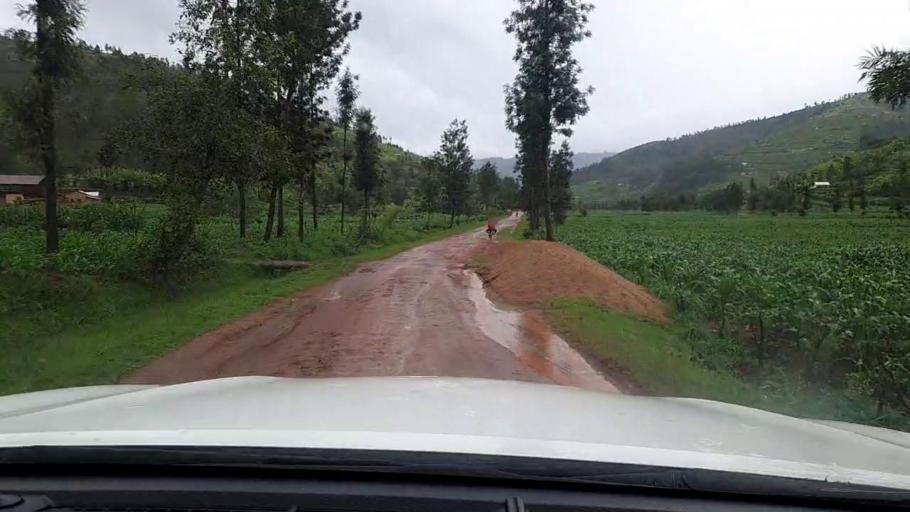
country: RW
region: Northern Province
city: Byumba
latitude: -1.7397
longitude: 29.9428
